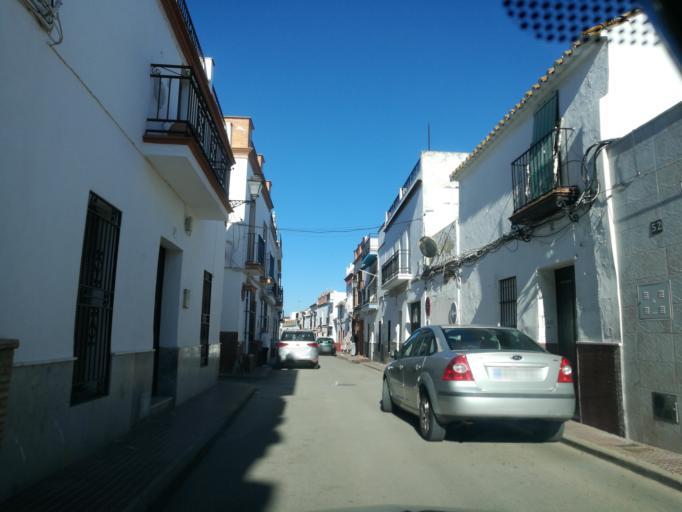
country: ES
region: Andalusia
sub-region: Provincia de Sevilla
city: La Campana
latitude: 37.5708
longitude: -5.4274
